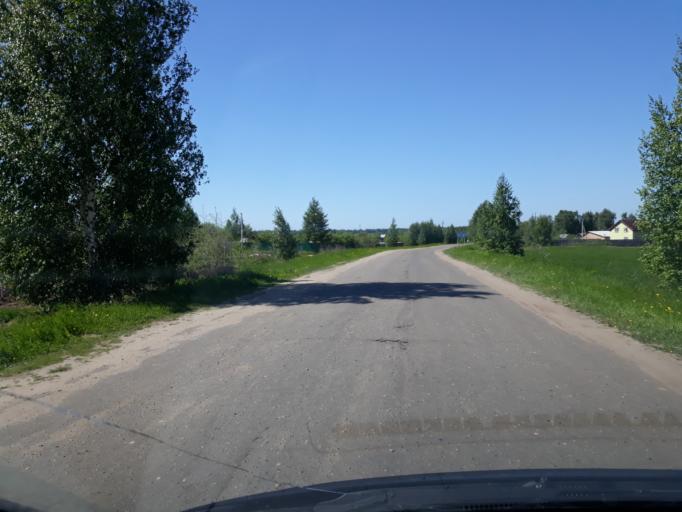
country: RU
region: Jaroslavl
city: Yaroslavl
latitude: 57.6727
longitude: 40.0271
